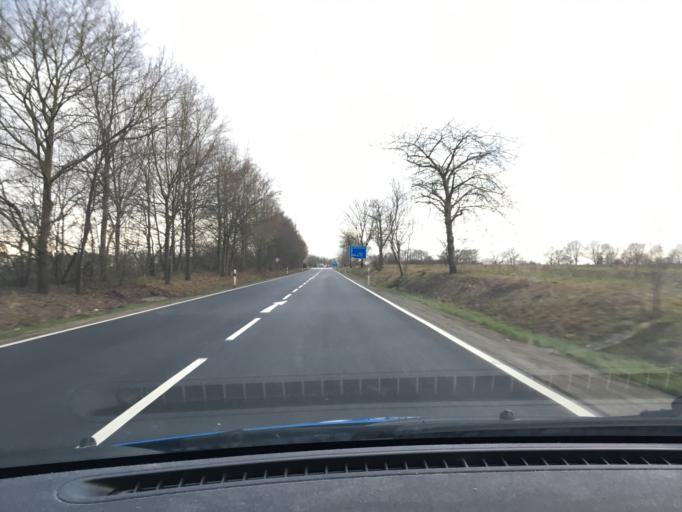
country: DE
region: Schleswig-Holstein
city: Lagerdorf
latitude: 53.8720
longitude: 9.5684
